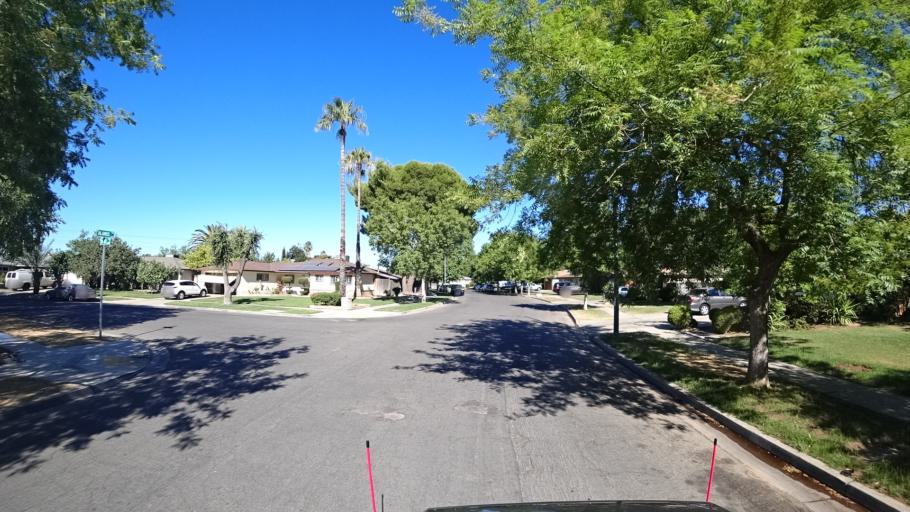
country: US
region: California
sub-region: Fresno County
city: West Park
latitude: 36.8057
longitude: -119.8487
